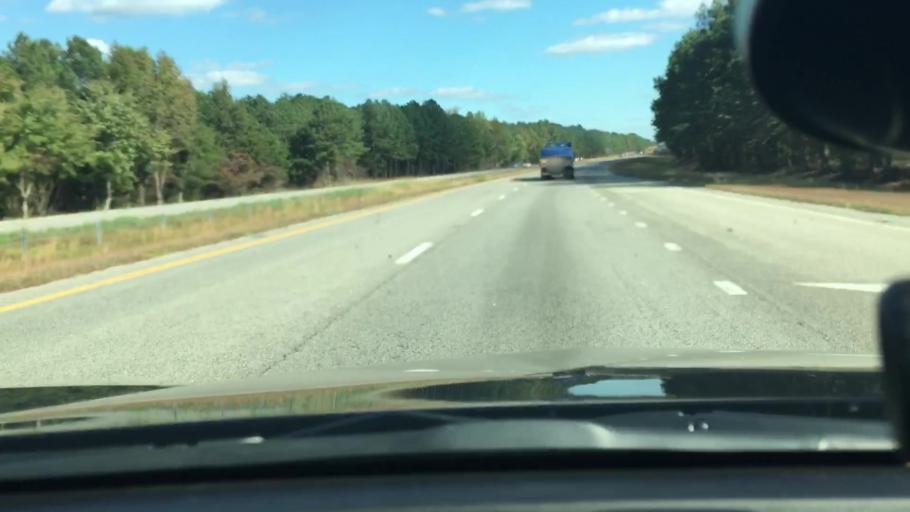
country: US
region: North Carolina
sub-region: Wilson County
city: Wilson
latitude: 35.6733
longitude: -77.7989
